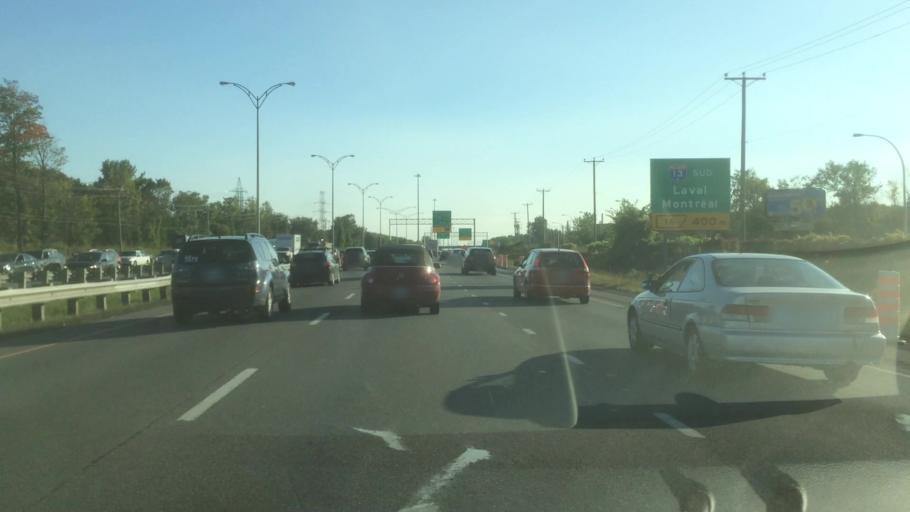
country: CA
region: Quebec
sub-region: Laurentides
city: Boisbriand
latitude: 45.6076
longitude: -73.8565
